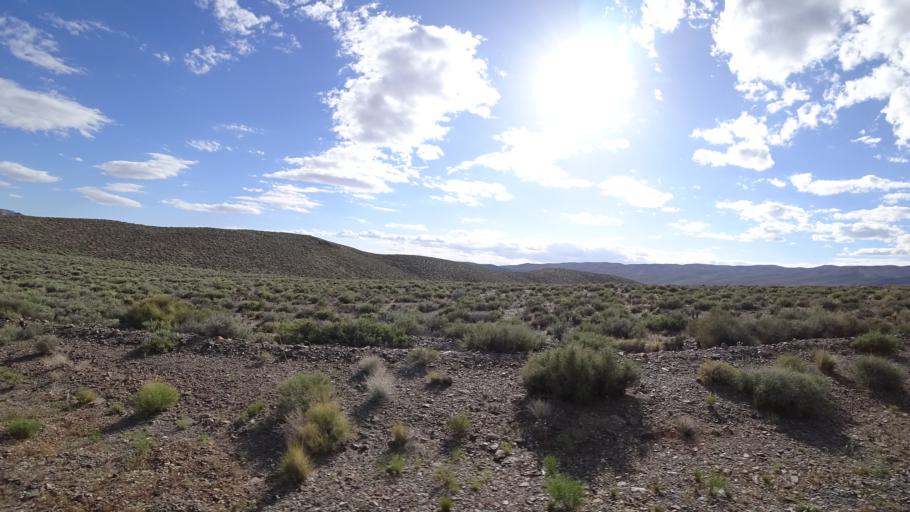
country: US
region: California
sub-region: San Bernardino County
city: Searles Valley
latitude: 36.3151
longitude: -117.1553
